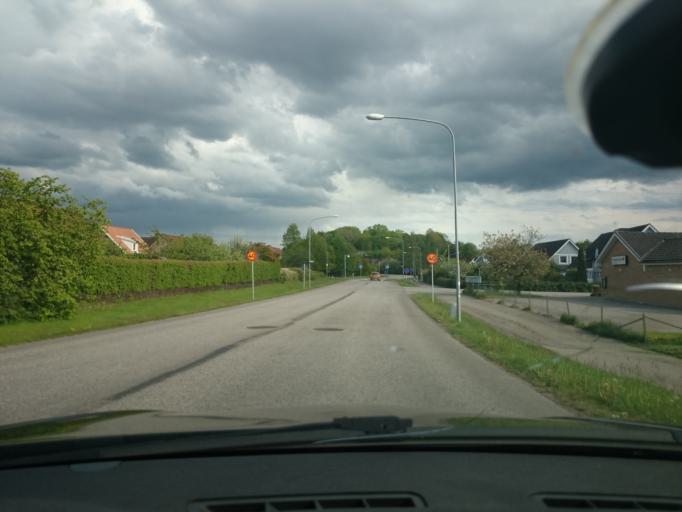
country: SE
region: OEstergoetland
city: Lindo
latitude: 58.5693
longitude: 16.2313
